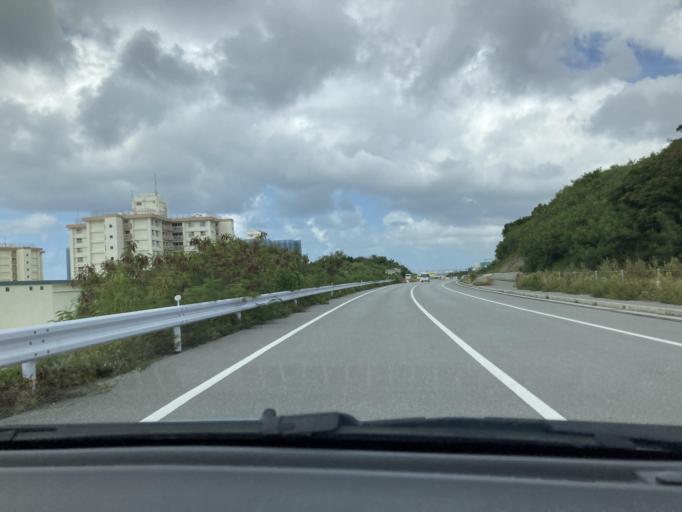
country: JP
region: Okinawa
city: Ginowan
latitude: 26.2650
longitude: 127.7088
